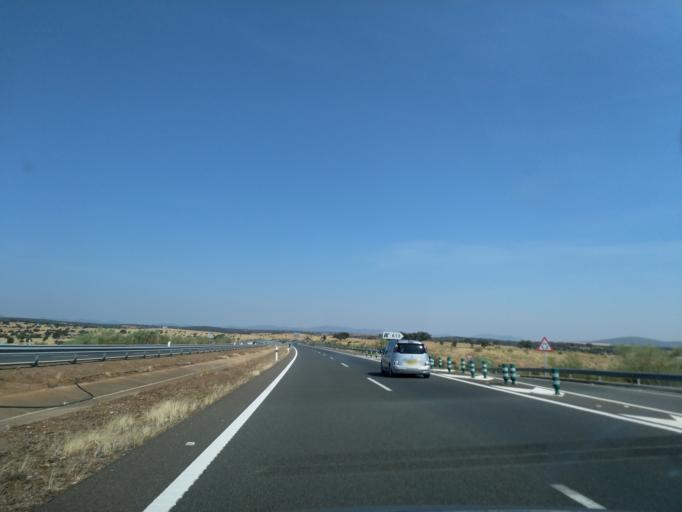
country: ES
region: Extremadura
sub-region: Provincia de Badajoz
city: Mirandilla
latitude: 38.9749
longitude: -6.3345
